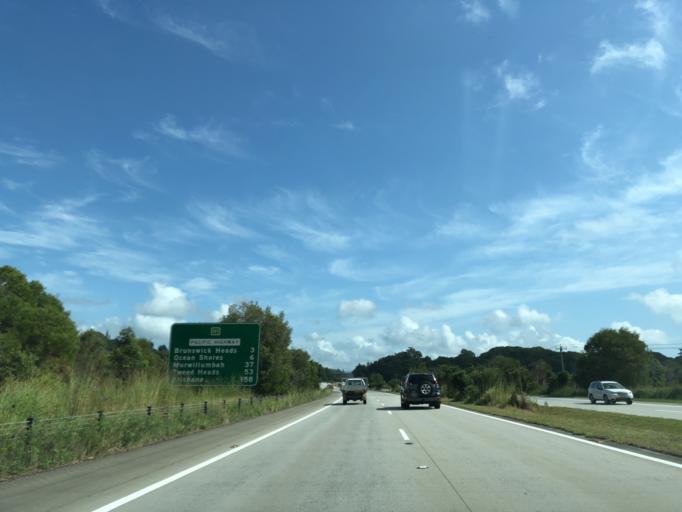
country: AU
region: New South Wales
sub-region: Byron Shire
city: Brunswick Heads
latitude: -28.5789
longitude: 153.5438
